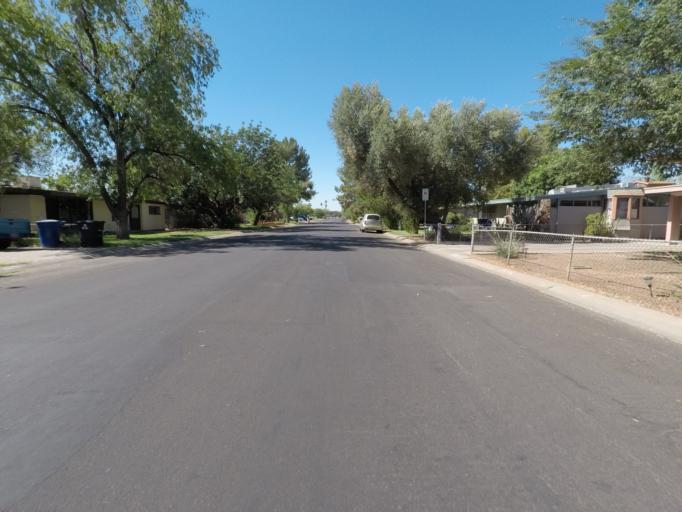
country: US
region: Arizona
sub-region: Maricopa County
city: Tempe Junction
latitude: 33.4125
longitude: -111.9443
